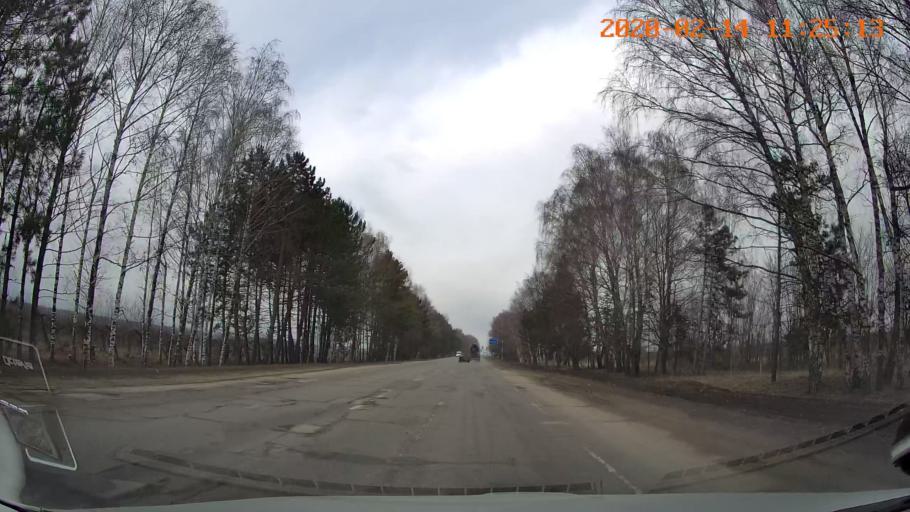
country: MD
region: Briceni
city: Briceni
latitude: 48.3470
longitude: 27.1055
